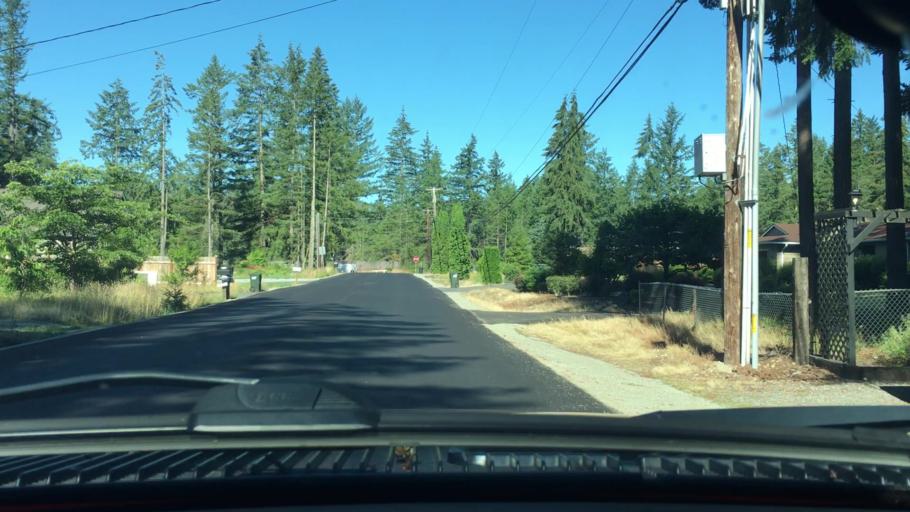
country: US
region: Washington
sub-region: King County
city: Lake Morton-Berrydale
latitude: 47.3175
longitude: -122.0999
